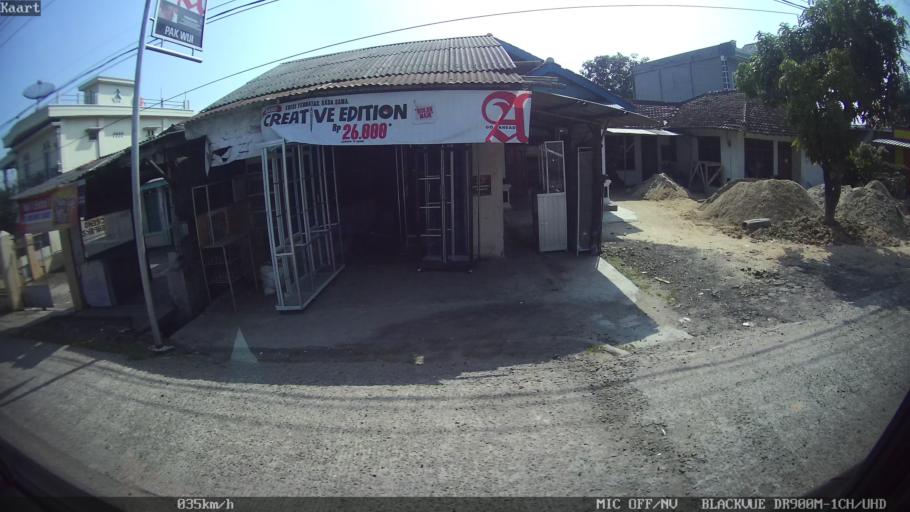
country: ID
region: Lampung
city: Natar
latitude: -5.2507
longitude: 105.1818
